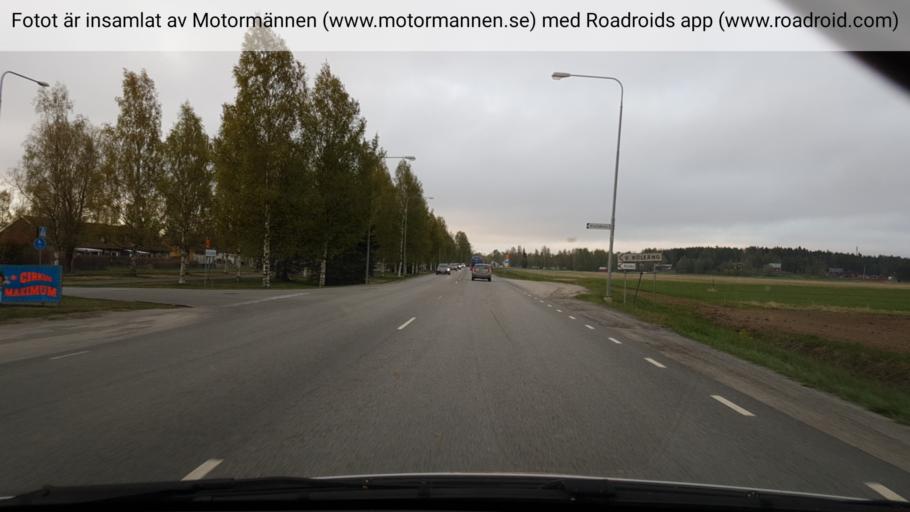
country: SE
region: Vaesterbotten
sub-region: Umea Kommun
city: Roback
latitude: 63.8133
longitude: 20.2154
